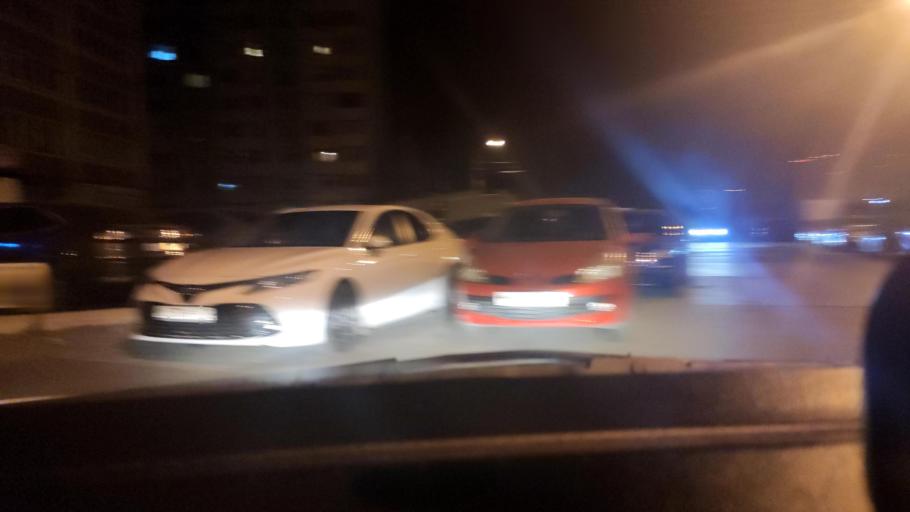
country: RU
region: Voronezj
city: Podgornoye
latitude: 51.7128
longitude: 39.1530
